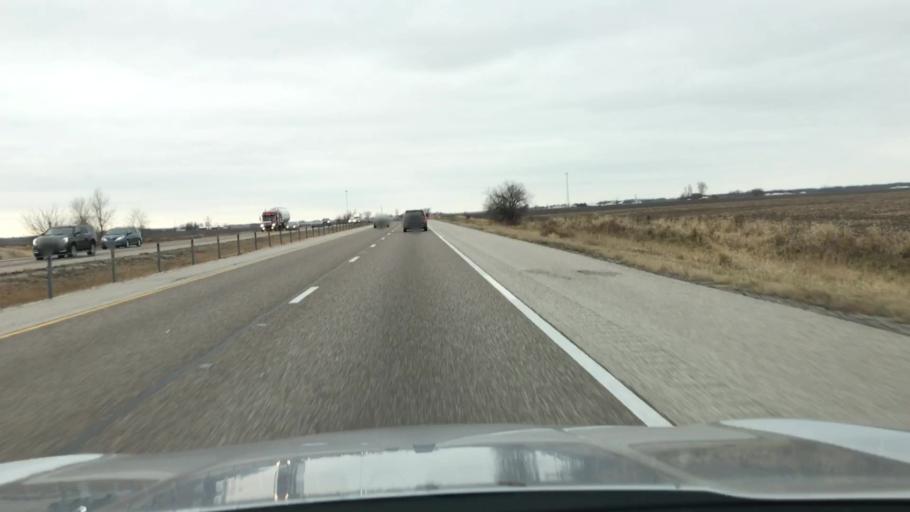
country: US
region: Illinois
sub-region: Madison County
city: Worden
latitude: 38.8479
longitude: -89.8672
